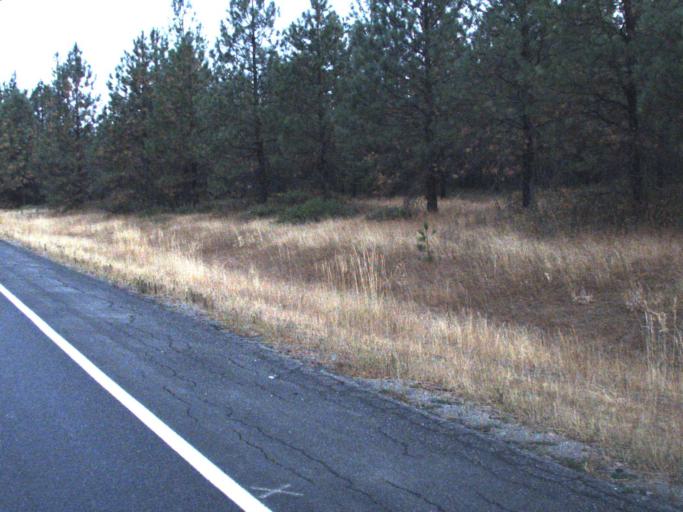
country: US
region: Washington
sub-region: Stevens County
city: Chewelah
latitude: 48.0667
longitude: -117.7003
